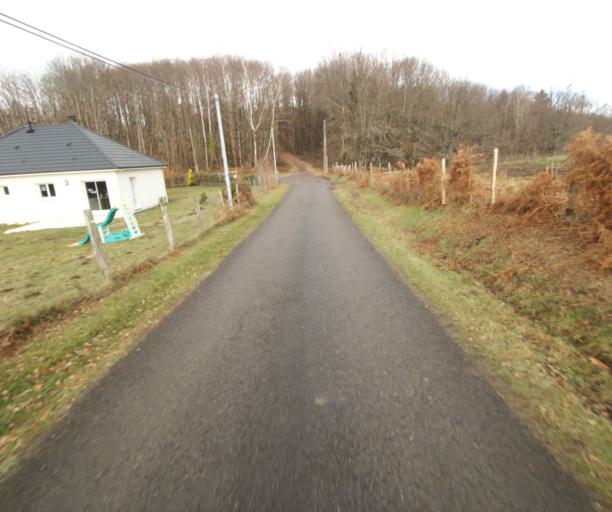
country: FR
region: Limousin
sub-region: Departement de la Correze
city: Saint-Mexant
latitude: 45.2799
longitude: 1.6483
